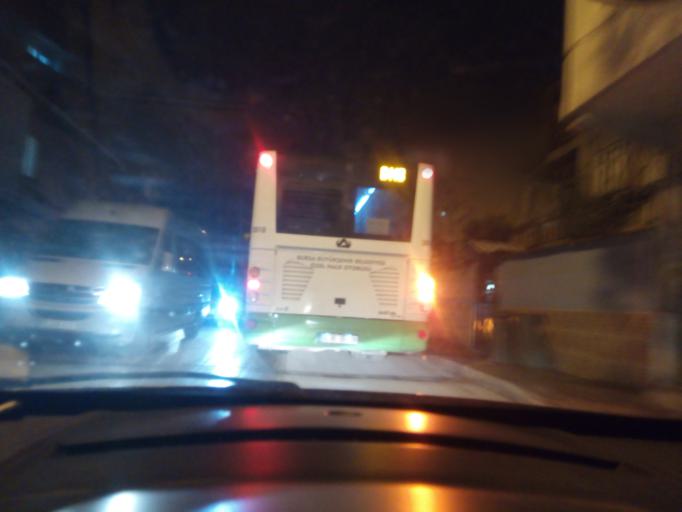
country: TR
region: Bursa
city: Niluefer
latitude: 40.2711
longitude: 28.9464
